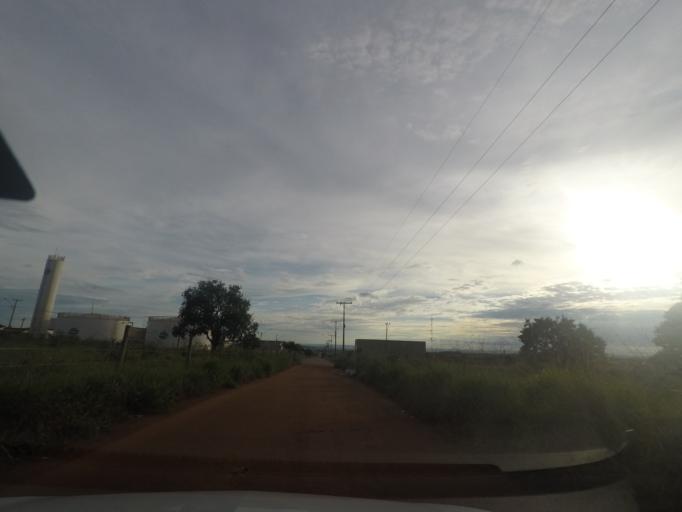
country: BR
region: Goias
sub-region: Trindade
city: Trindade
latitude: -16.7304
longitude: -49.4114
